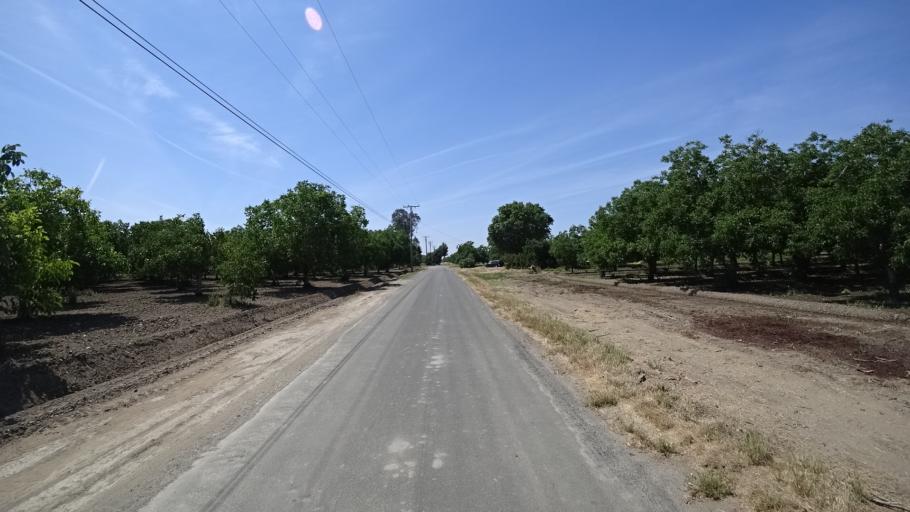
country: US
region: California
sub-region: Kings County
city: Armona
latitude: 36.3386
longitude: -119.7000
